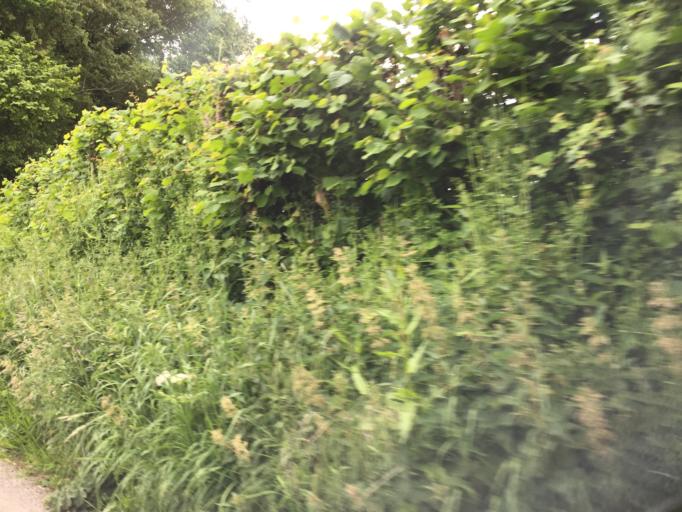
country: GB
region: England
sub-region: Wiltshire
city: Hankerton
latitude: 51.6495
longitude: -2.0152
